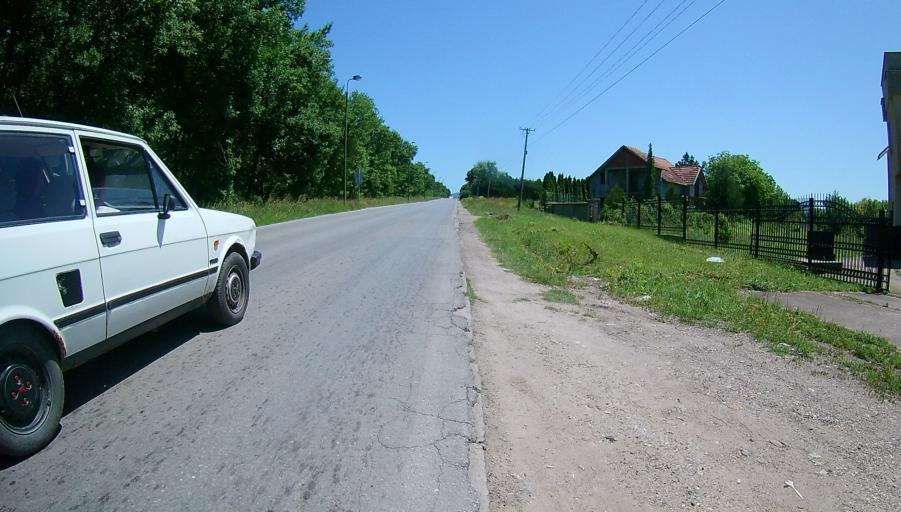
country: RS
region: Central Serbia
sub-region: Nisavski Okrug
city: Nis
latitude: 43.3046
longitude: 21.8685
